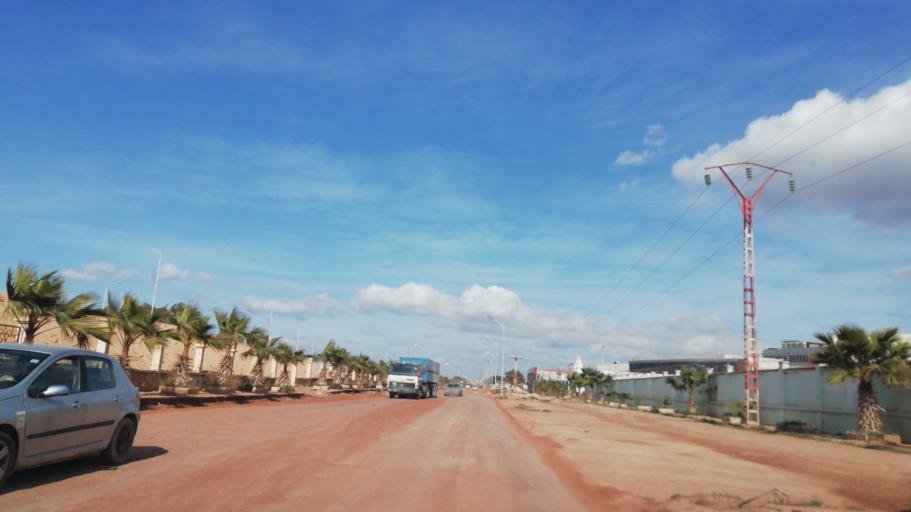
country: DZ
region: Oran
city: Es Senia
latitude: 35.6253
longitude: -0.5842
